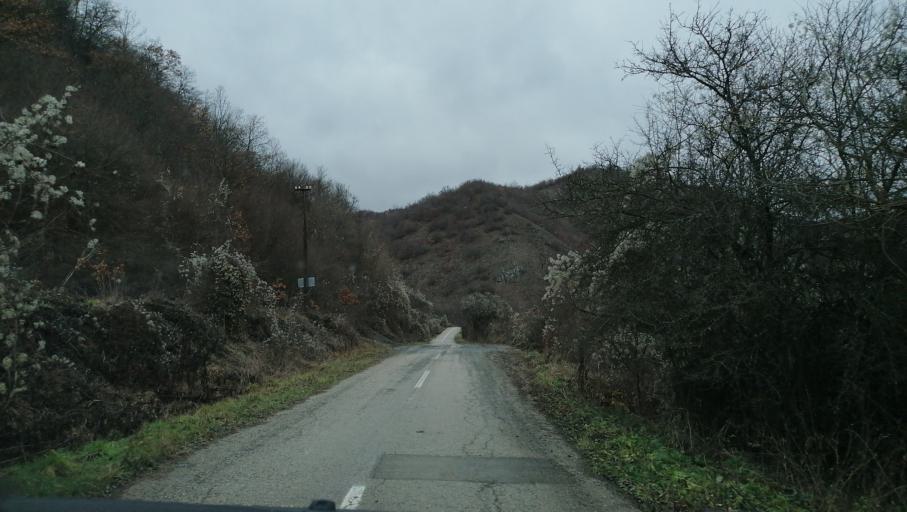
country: RS
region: Central Serbia
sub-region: Pirotski Okrug
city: Dimitrovgrad
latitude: 42.9463
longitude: 22.7674
